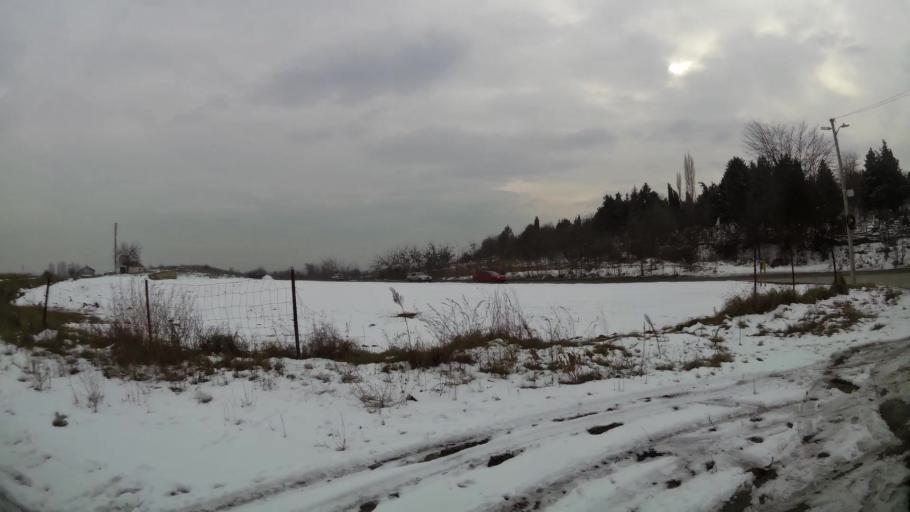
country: MK
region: Suto Orizari
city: Suto Orizare
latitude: 42.0428
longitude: 21.4376
